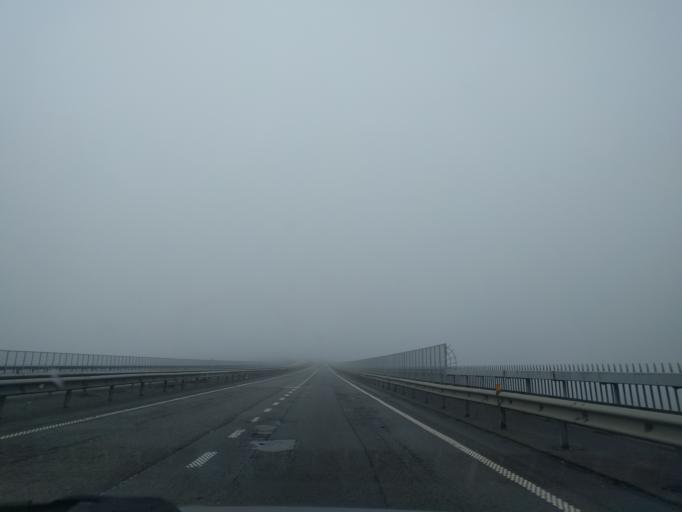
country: BE
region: Wallonia
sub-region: Province de Namur
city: Dinant
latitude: 50.2407
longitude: 4.9211
